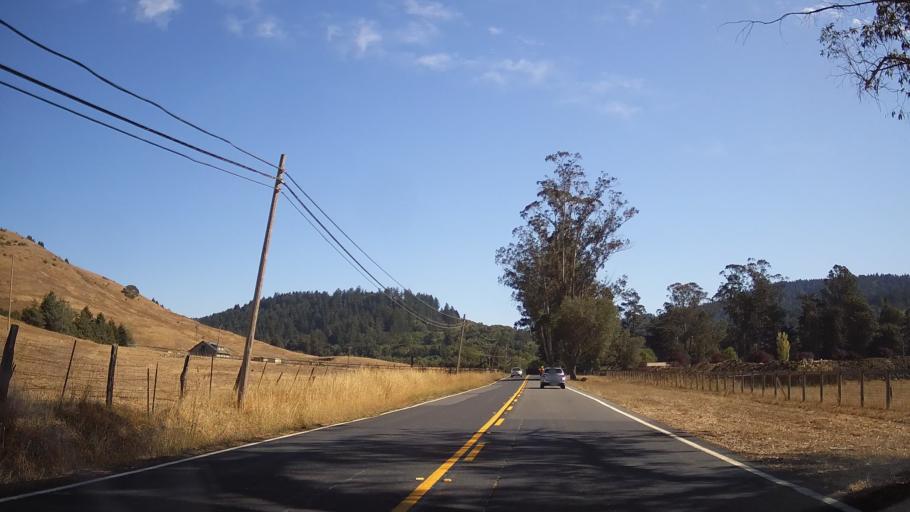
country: US
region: California
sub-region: Marin County
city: Lagunitas-Forest Knolls
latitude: 38.0580
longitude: -122.6958
